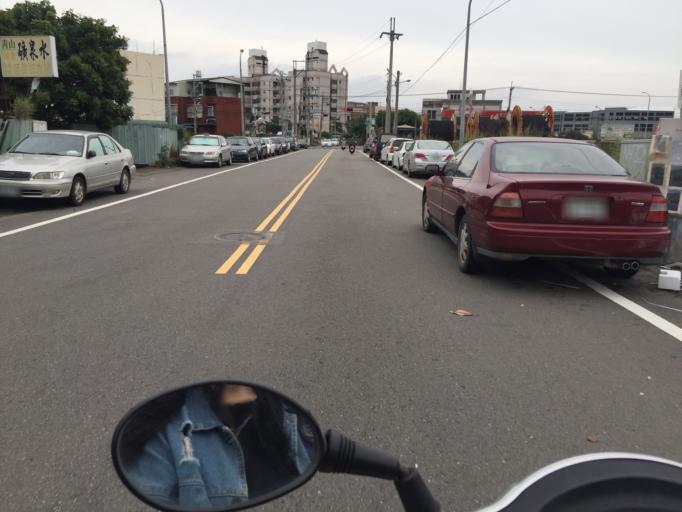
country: TW
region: Taiwan
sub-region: Taichung City
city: Taichung
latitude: 24.0758
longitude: 120.7163
